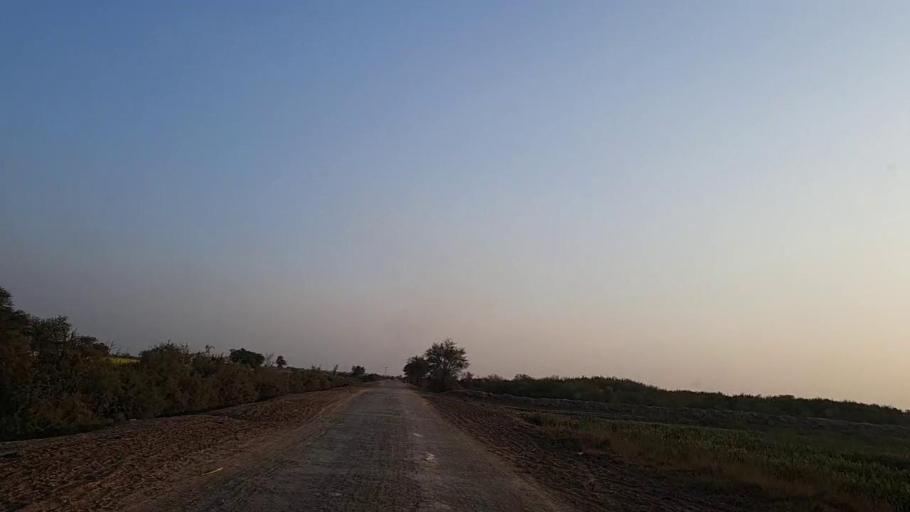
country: PK
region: Sindh
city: Shahdadpur
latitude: 25.9925
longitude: 68.4942
